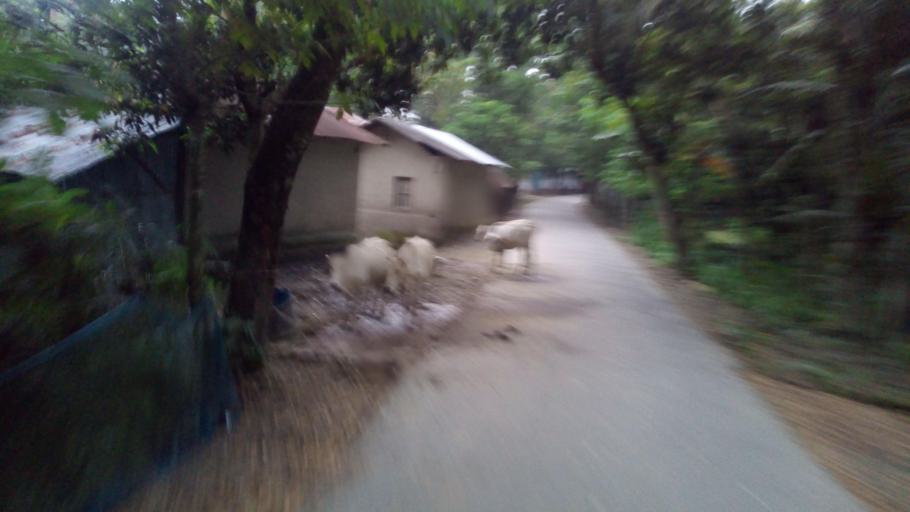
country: BD
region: Khulna
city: Phultala
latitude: 22.7588
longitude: 89.4081
